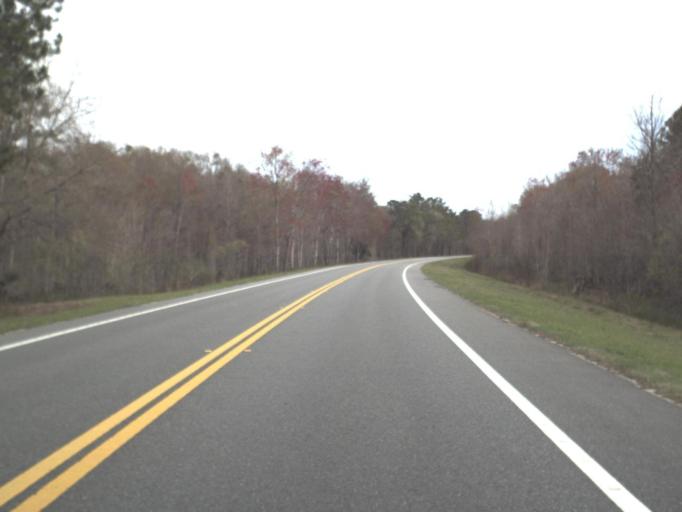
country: US
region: Florida
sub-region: Leon County
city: Woodville
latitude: 30.1822
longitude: -84.0137
